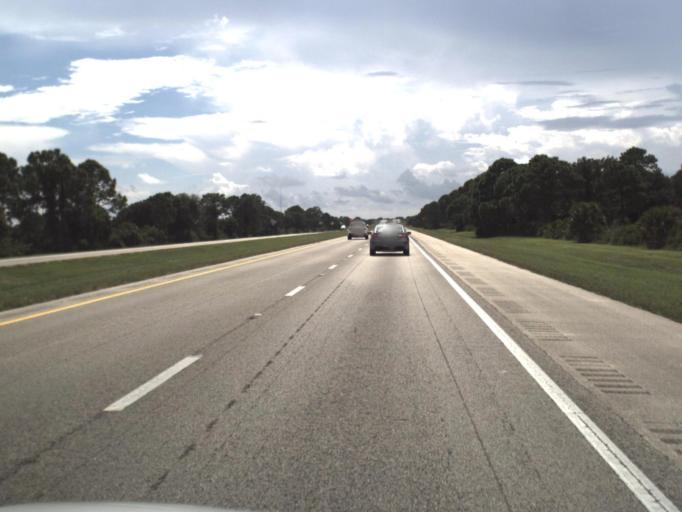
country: US
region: Florida
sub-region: Sarasota County
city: Laurel
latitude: 27.1817
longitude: -82.4459
